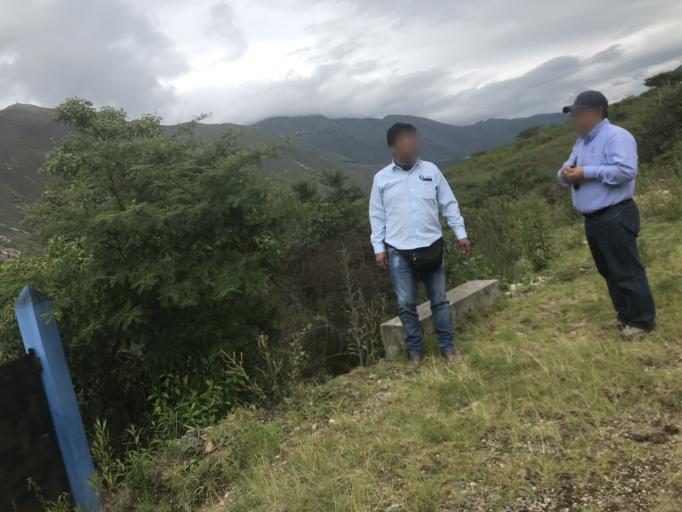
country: PE
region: Amazonas
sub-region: Provincia de Chachapoyas
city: Magdalena
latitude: -6.3996
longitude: -77.8850
